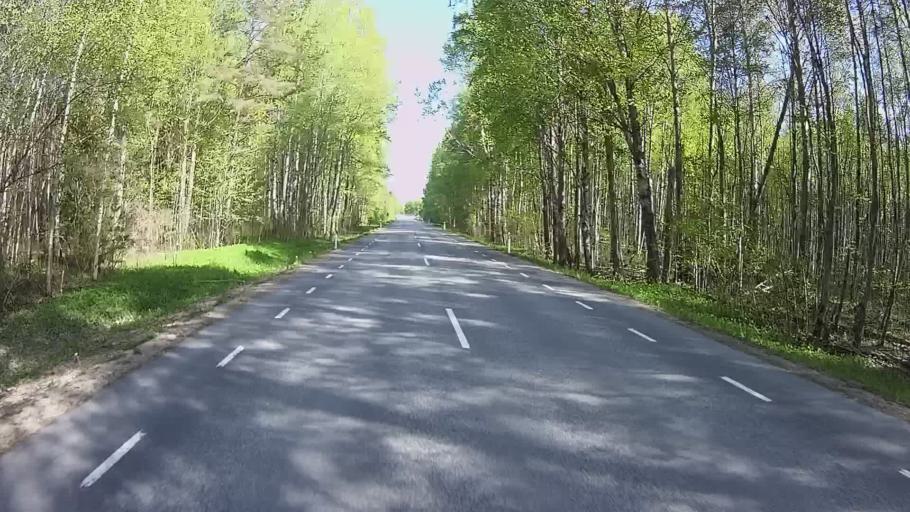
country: EE
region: Polvamaa
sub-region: Raepina vald
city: Rapina
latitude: 58.0505
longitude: 27.5543
